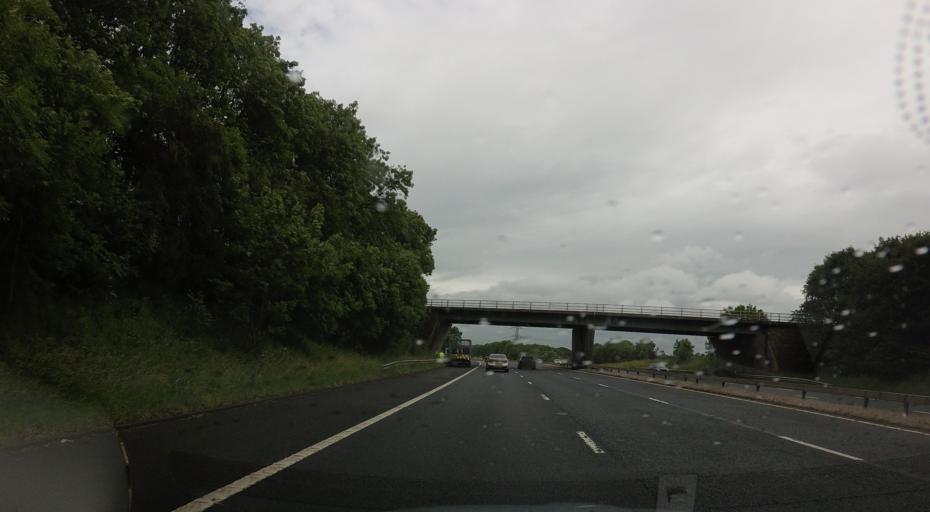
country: GB
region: England
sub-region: Cumbria
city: Scotby
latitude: 54.8674
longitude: -2.8759
